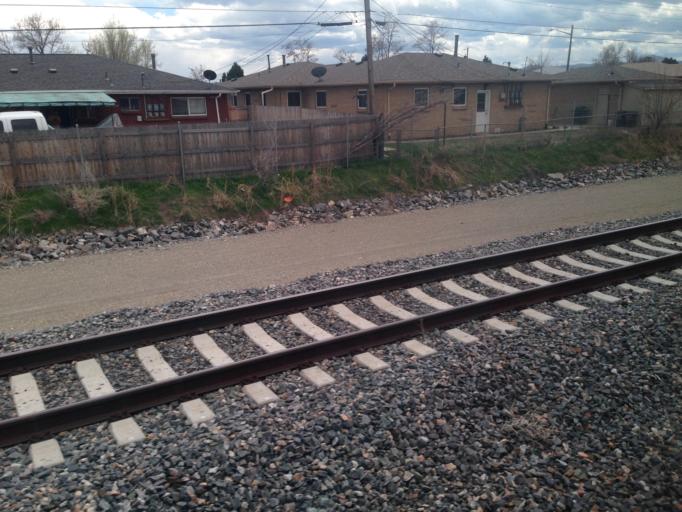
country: US
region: Colorado
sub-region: Jefferson County
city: Arvada
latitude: 39.7957
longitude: -105.0938
